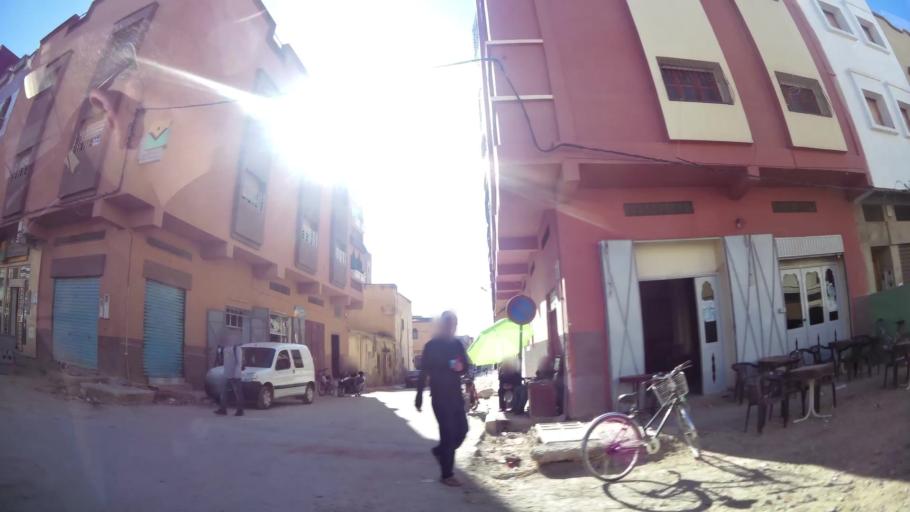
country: MA
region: Oriental
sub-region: Berkane-Taourirt
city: Ahfir
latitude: 34.9532
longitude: -2.0995
